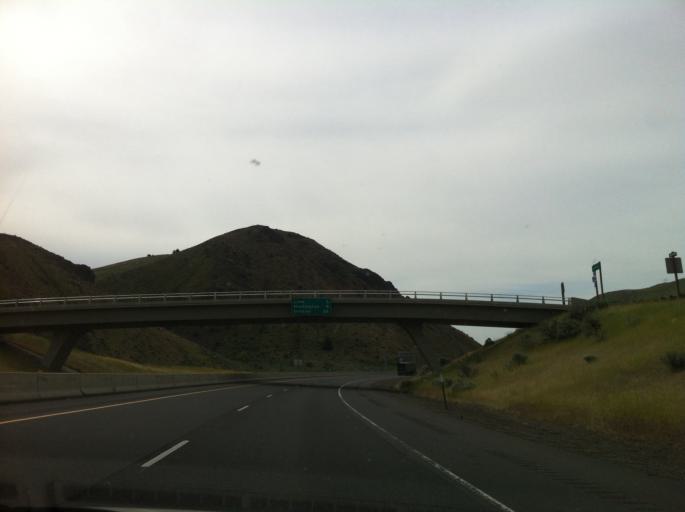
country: US
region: Idaho
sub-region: Washington County
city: Weiser
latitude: 44.4457
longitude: -117.3268
